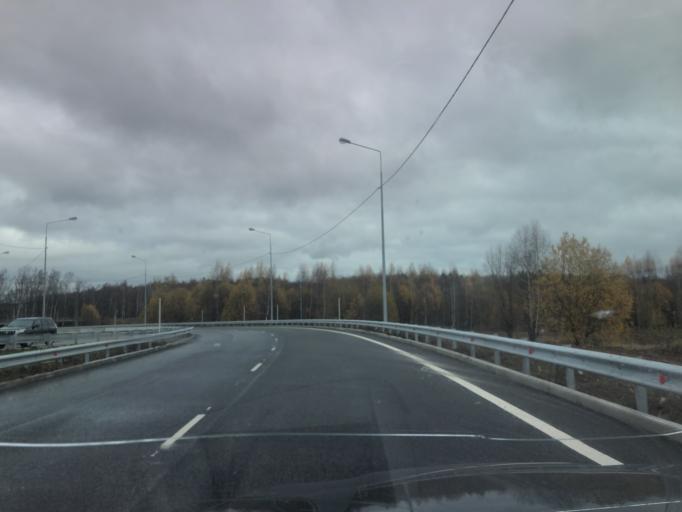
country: RU
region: Moskovskaya
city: Sergiyev Posad
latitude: 56.3425
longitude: 38.1270
